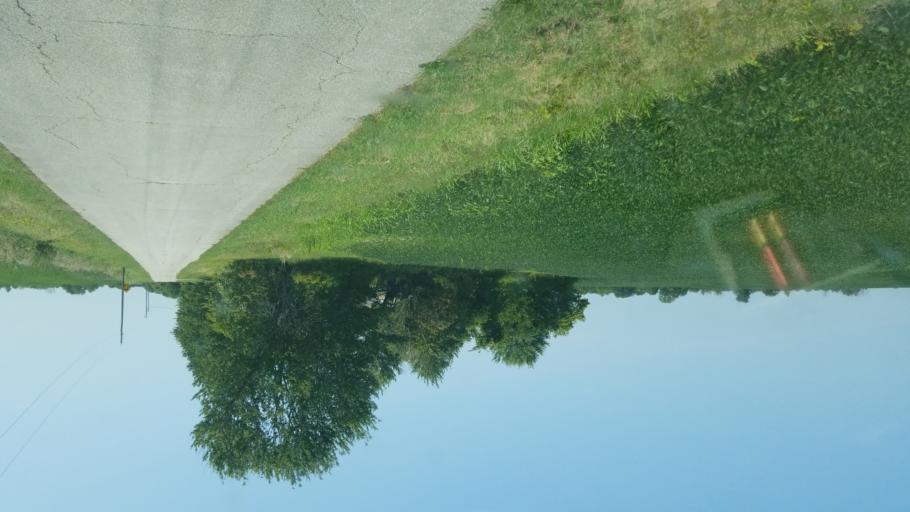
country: US
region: Ohio
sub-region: Crawford County
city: Bucyrus
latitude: 40.8491
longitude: -83.1055
